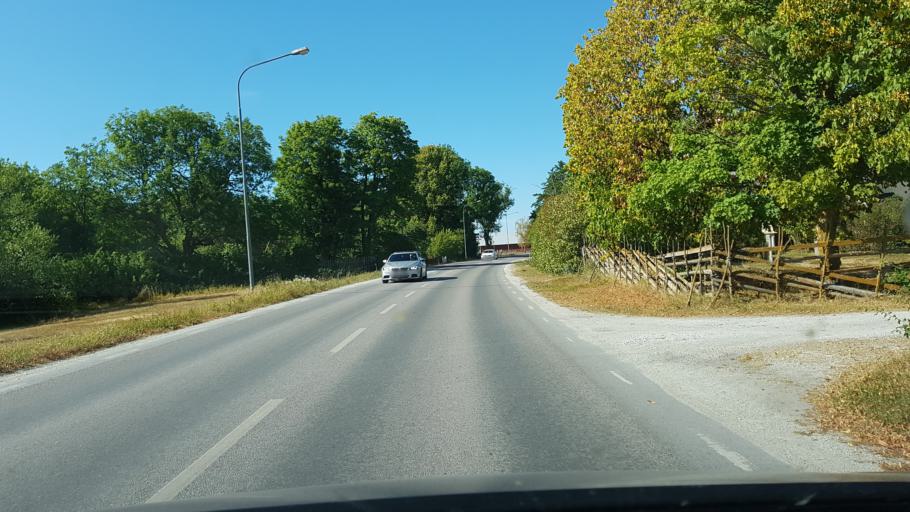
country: SE
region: Gotland
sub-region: Gotland
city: Klintehamn
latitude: 57.4374
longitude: 18.1448
